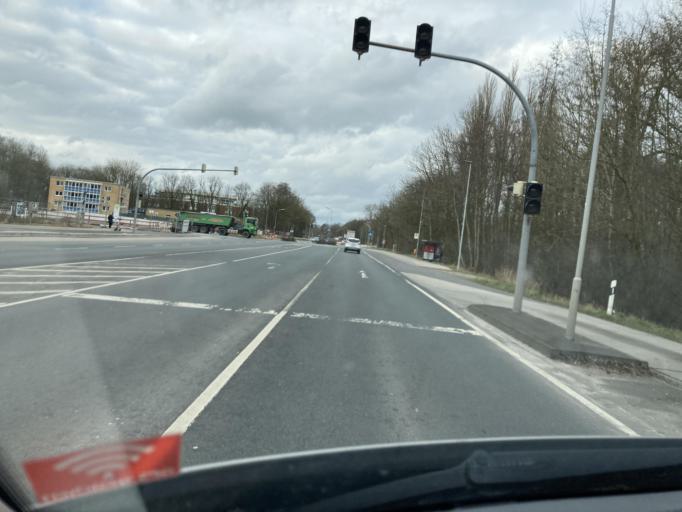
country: DE
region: Lower Saxony
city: Wilhelmshaven
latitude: 53.5452
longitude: 8.0861
